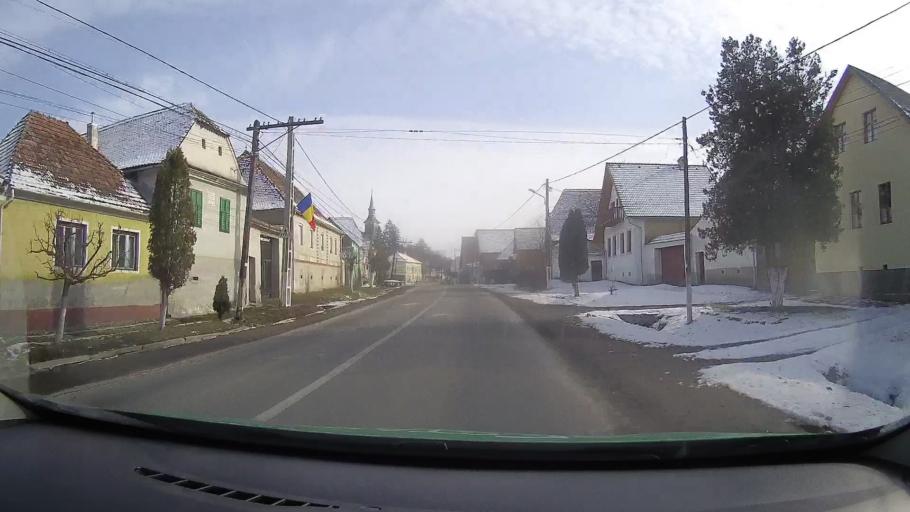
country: RO
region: Mures
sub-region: Comuna Apold
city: Saes
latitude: 46.1574
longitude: 24.7670
